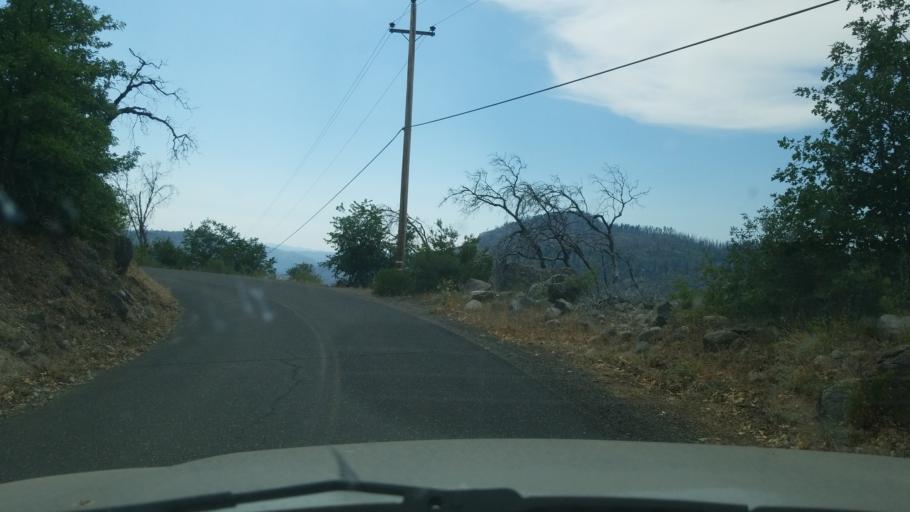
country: US
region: California
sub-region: Mariposa County
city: Yosemite Valley
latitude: 37.8949
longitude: -119.8447
